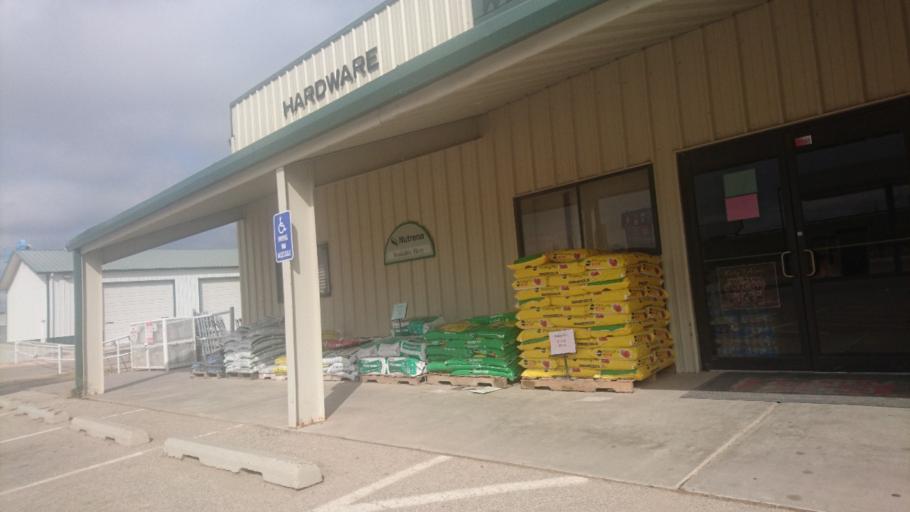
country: US
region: Texas
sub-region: Potter County
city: Bushland
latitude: 35.1925
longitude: -102.0643
